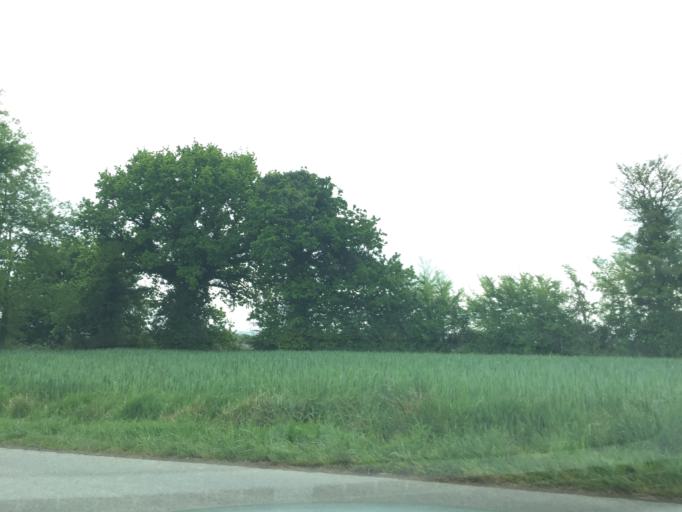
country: FR
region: Brittany
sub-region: Departement des Cotes-d'Armor
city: Crehen
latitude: 48.5857
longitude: -2.2208
